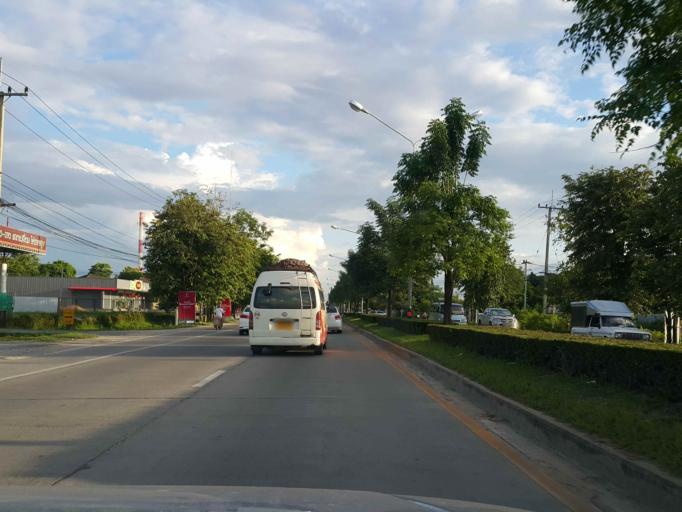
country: TH
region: Chiang Mai
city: San Sai
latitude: 18.8454
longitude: 99.0136
